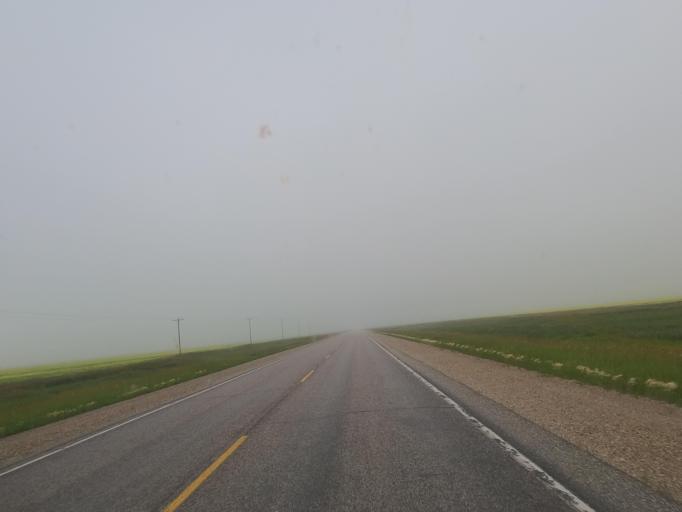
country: CA
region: Manitoba
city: Carman
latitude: 49.7040
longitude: -97.9347
